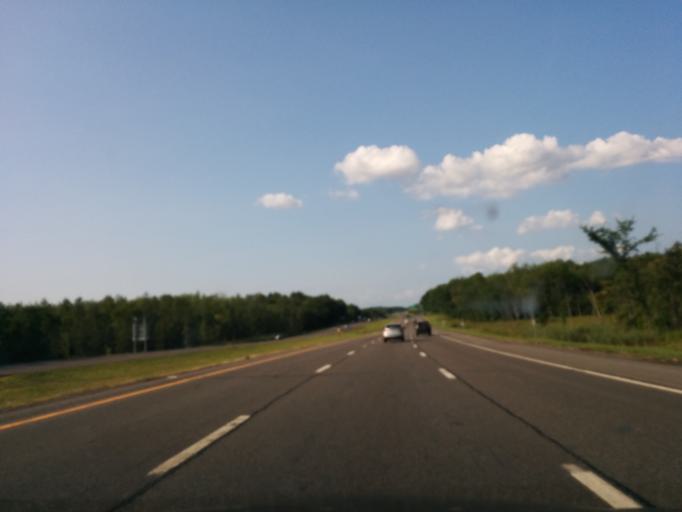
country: US
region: New York
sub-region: Oswego County
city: Central Square
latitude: 43.2706
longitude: -76.1306
